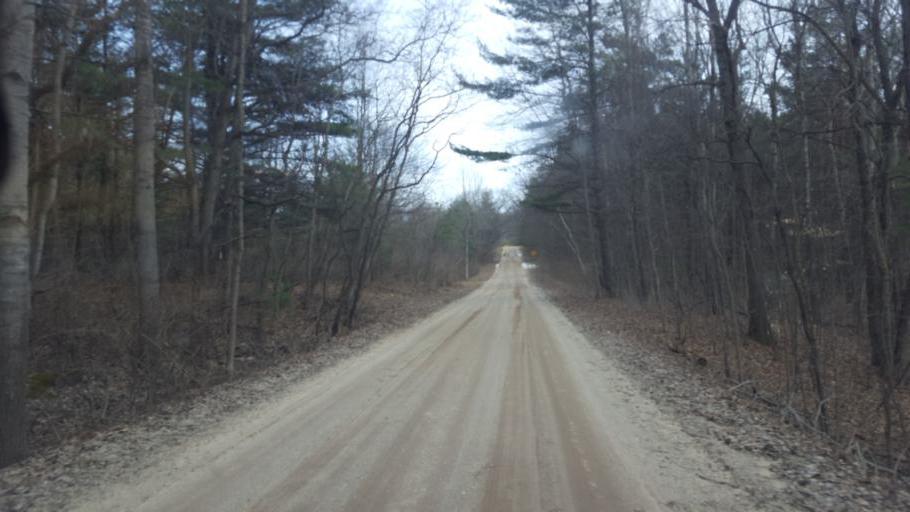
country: US
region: Michigan
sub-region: Isabella County
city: Lake Isabella
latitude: 43.6791
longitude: -85.1307
